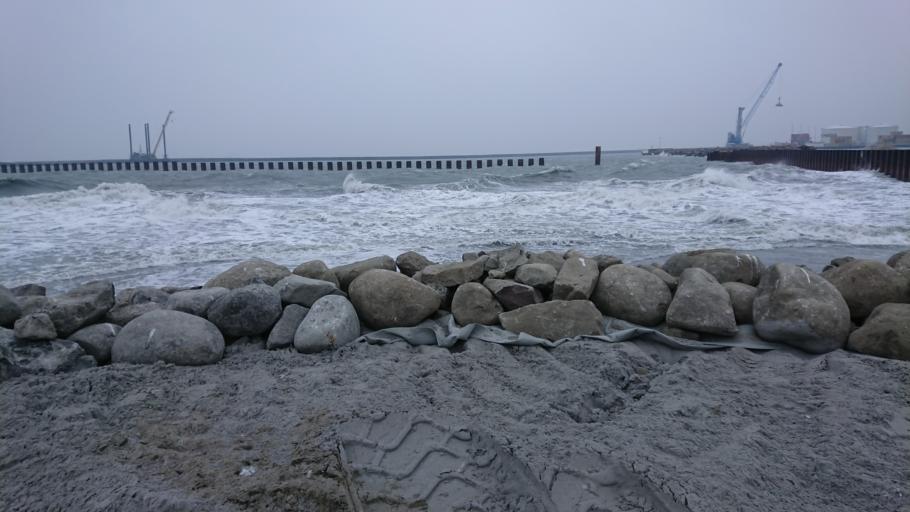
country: DK
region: North Denmark
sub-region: Frederikshavn Kommune
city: Skagen
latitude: 57.7167
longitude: 10.5994
